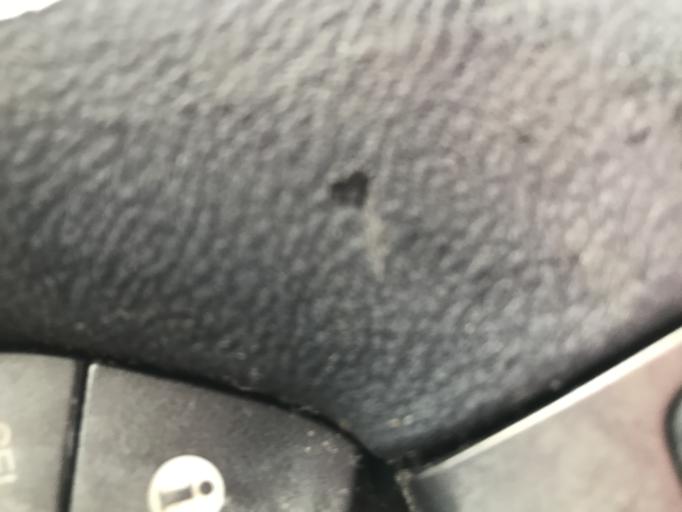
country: US
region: Louisiana
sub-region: Orleans Parish
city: New Orleans
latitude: 29.9520
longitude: -90.0877
